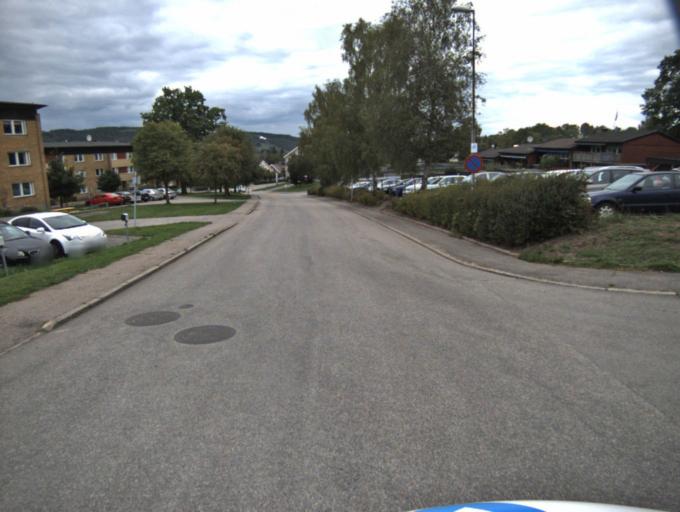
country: SE
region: Vaestra Goetaland
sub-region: Ulricehamns Kommun
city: Ulricehamn
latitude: 57.7972
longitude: 13.4250
